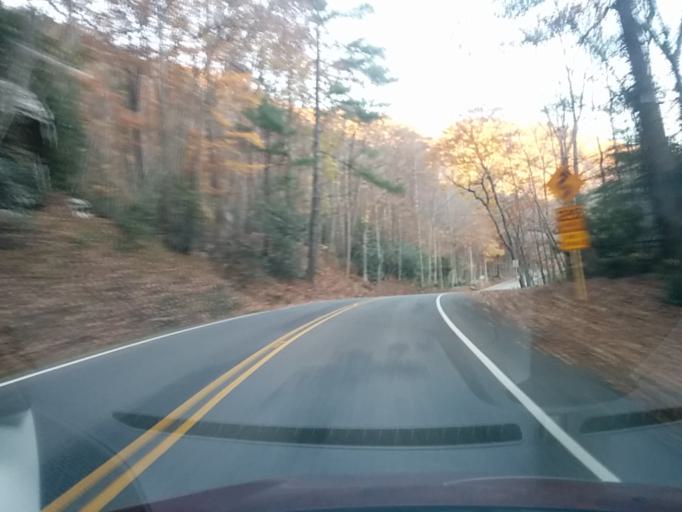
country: US
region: Virginia
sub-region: Rockbridge County
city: East Lexington
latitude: 37.9303
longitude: -79.4559
